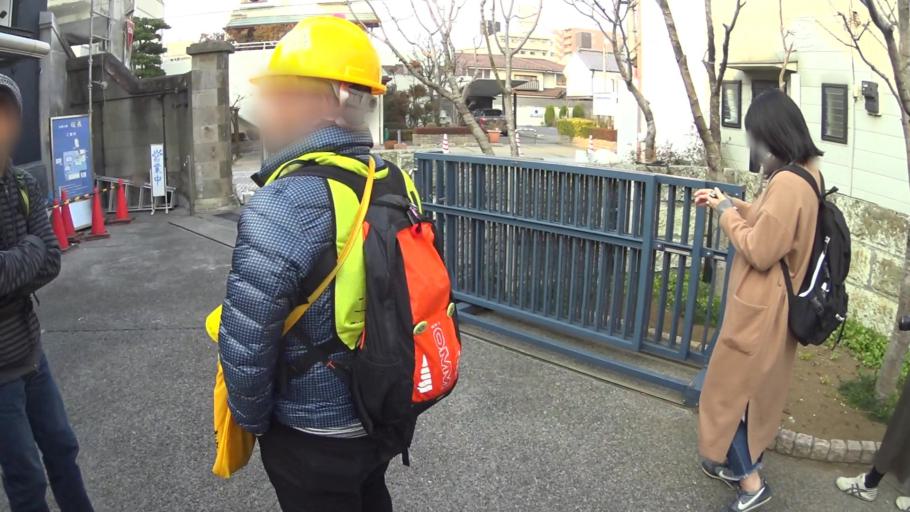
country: JP
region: Ibaraki
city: Koga
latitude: 36.1939
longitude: 139.7044
